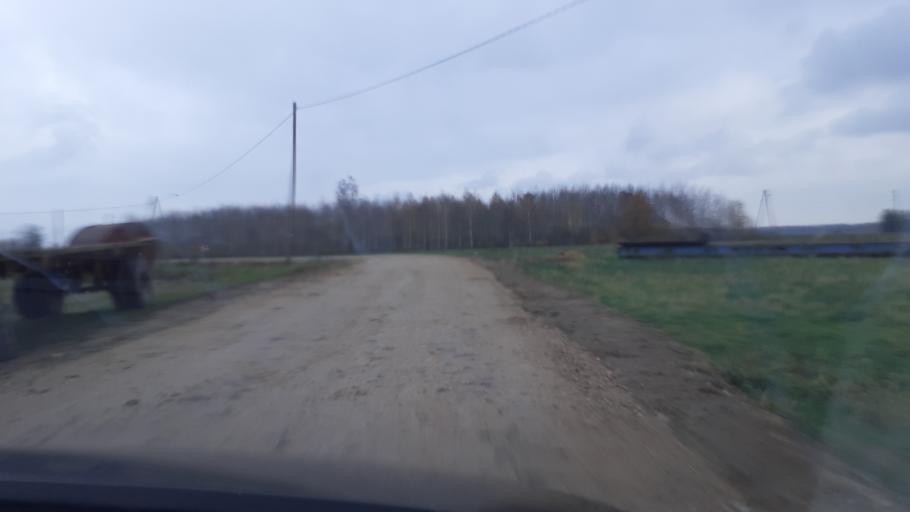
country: LV
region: Talsu Rajons
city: Sabile
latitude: 56.9405
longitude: 22.4201
